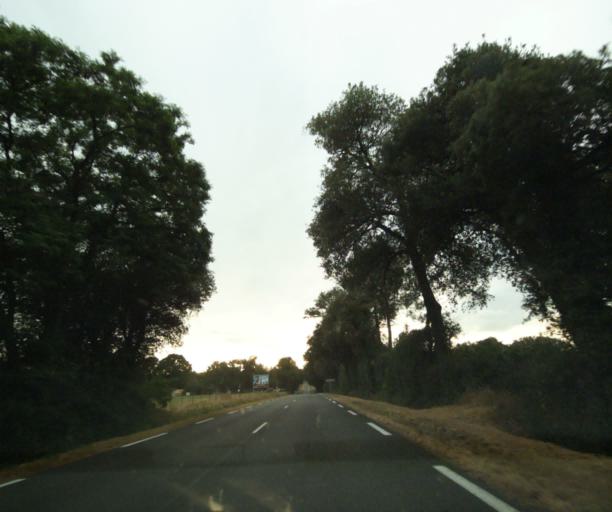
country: FR
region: Pays de la Loire
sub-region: Departement de la Vendee
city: Avrille
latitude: 46.4735
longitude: -1.5048
